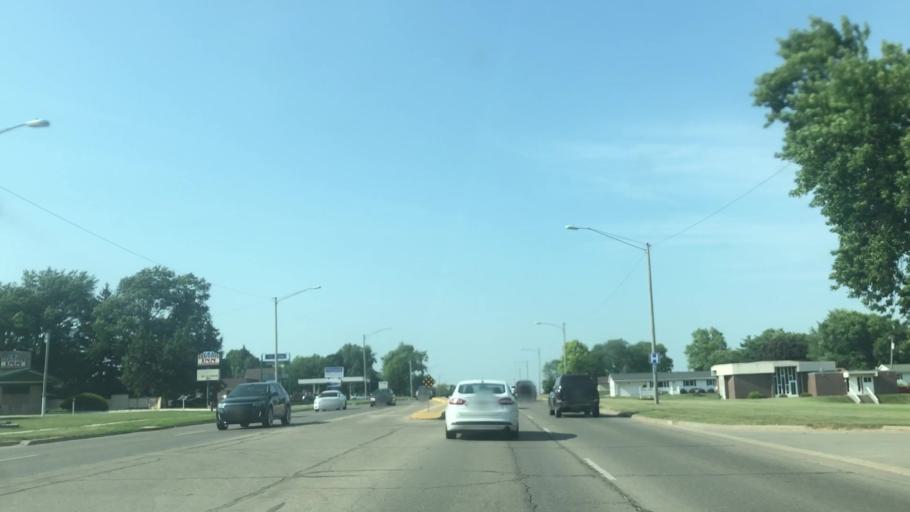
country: US
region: Iowa
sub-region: Marshall County
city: Marshalltown
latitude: 42.0219
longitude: -92.9124
